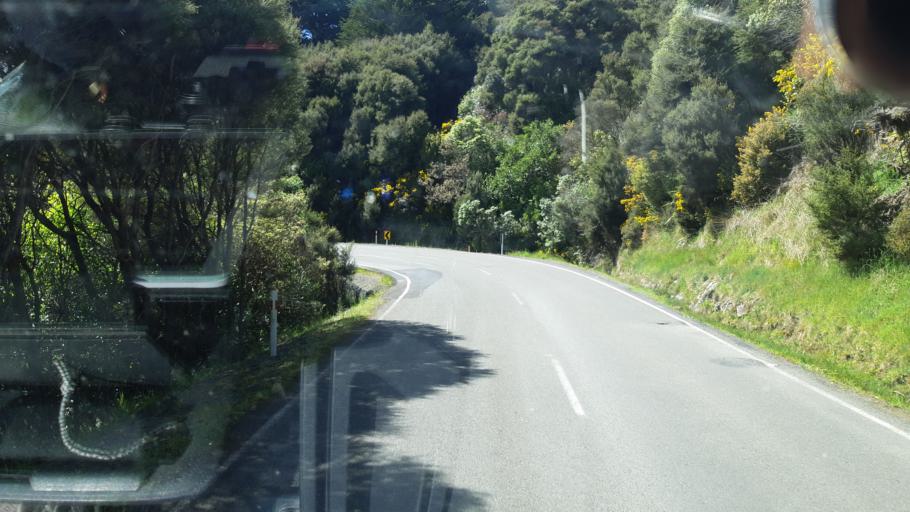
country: NZ
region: Otago
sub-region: Dunedin City
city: Portobello
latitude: -45.7809
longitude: 170.5986
